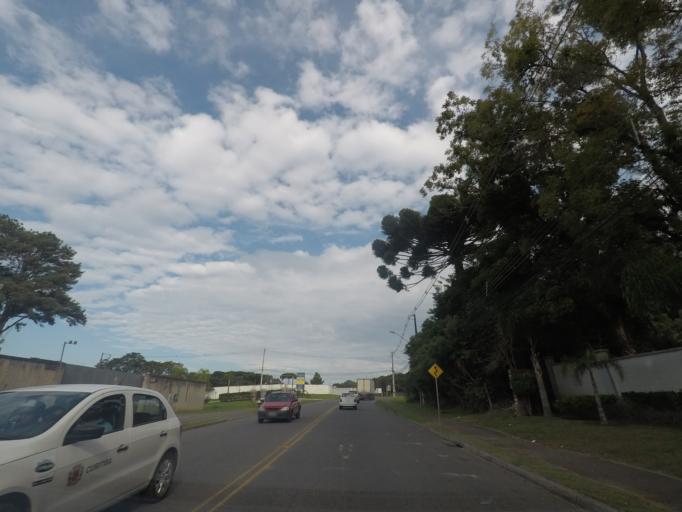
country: BR
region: Parana
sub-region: Sao Jose Dos Pinhais
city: Sao Jose dos Pinhais
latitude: -25.5570
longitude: -49.2922
